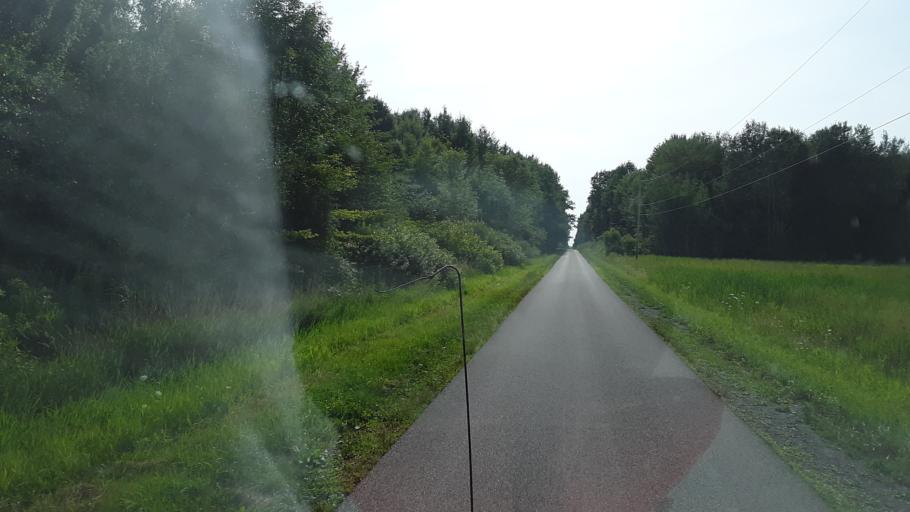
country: US
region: Ohio
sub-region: Ashtabula County
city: Andover
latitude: 41.6906
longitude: -80.6154
